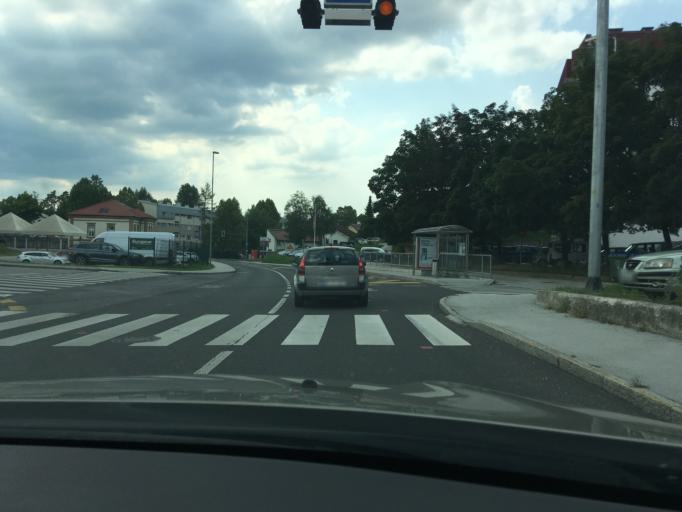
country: SI
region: Novo Mesto
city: Novo Mesto
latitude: 45.8000
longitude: 15.1751
